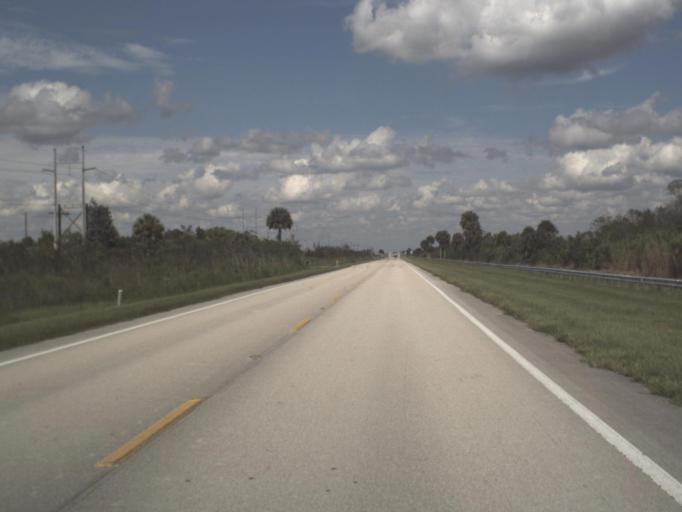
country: US
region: Florida
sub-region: Collier County
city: Orangetree
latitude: 26.1375
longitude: -81.3449
